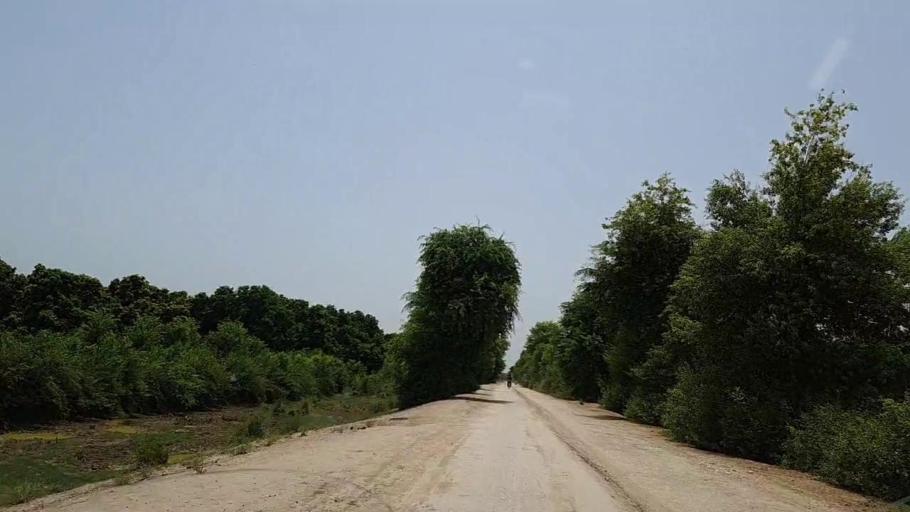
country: PK
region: Sindh
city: Tharu Shah
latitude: 27.0055
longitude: 68.1236
